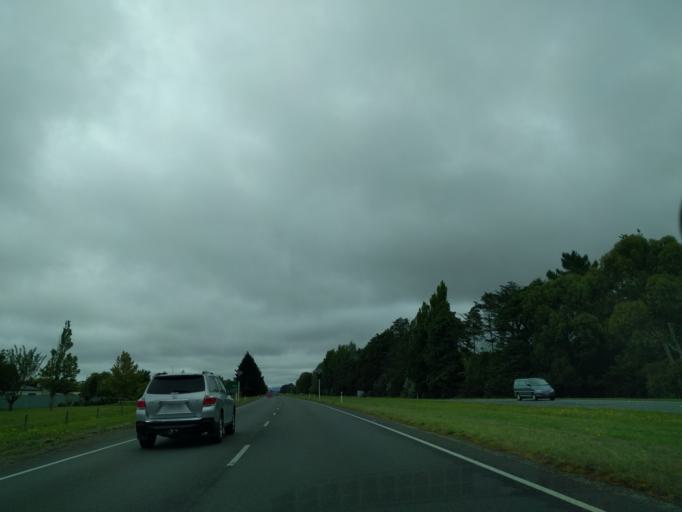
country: NZ
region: Canterbury
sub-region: Waimakariri District
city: Kaiapoi
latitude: -43.3924
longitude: 172.6402
